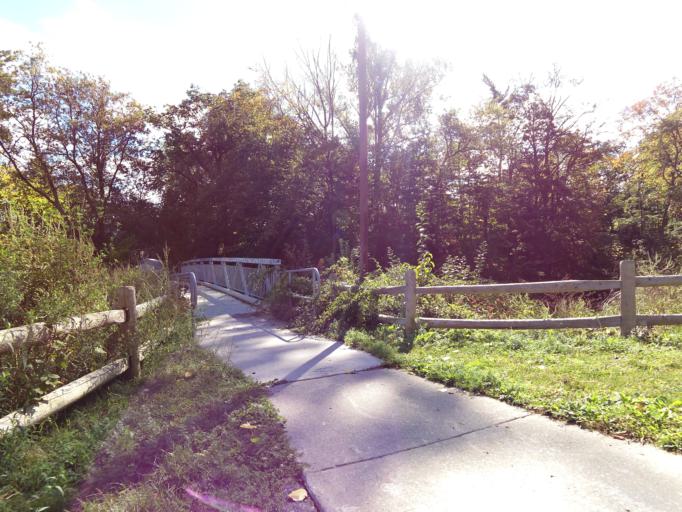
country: CA
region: Ontario
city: Ajax
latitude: 43.8221
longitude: -79.0997
